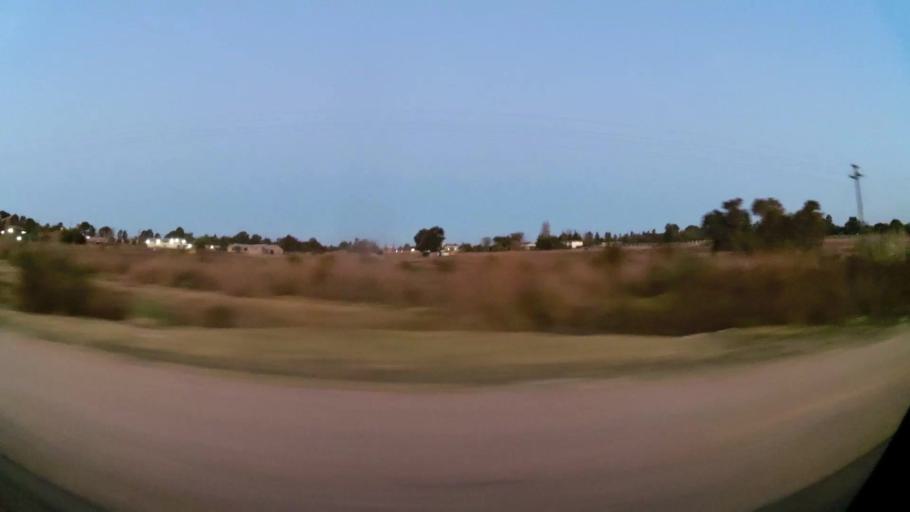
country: ZA
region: Gauteng
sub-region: City of Johannesburg Metropolitan Municipality
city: Midrand
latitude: -25.9477
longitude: 28.0908
